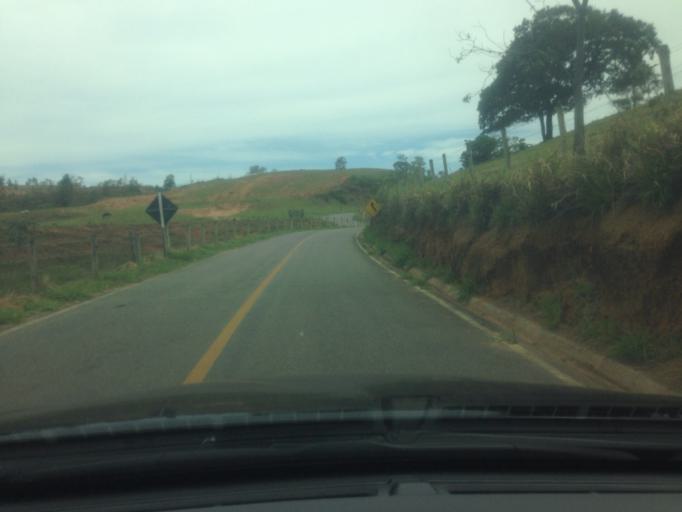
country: BR
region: Espirito Santo
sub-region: Guarapari
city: Guarapari
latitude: -20.6236
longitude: -40.5277
